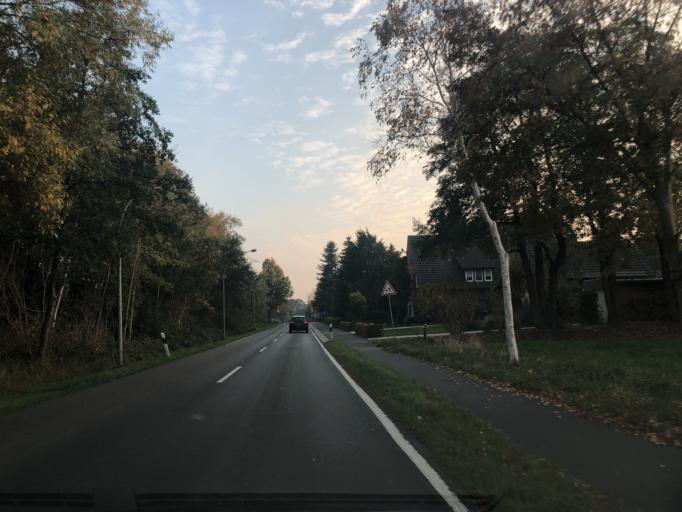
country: DE
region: Lower Saxony
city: Wardenburg
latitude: 53.0685
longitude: 8.1641
